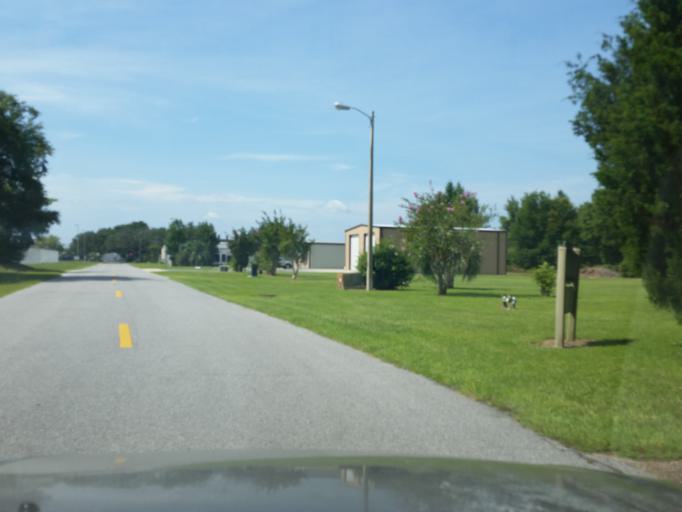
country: US
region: Florida
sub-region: Escambia County
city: Ferry Pass
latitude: 30.5325
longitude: -87.2002
